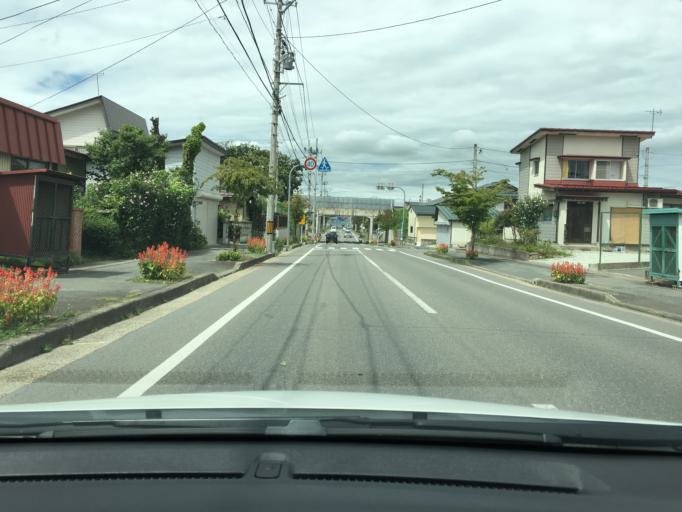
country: JP
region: Yamagata
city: Yonezawa
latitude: 37.8963
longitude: 140.1250
